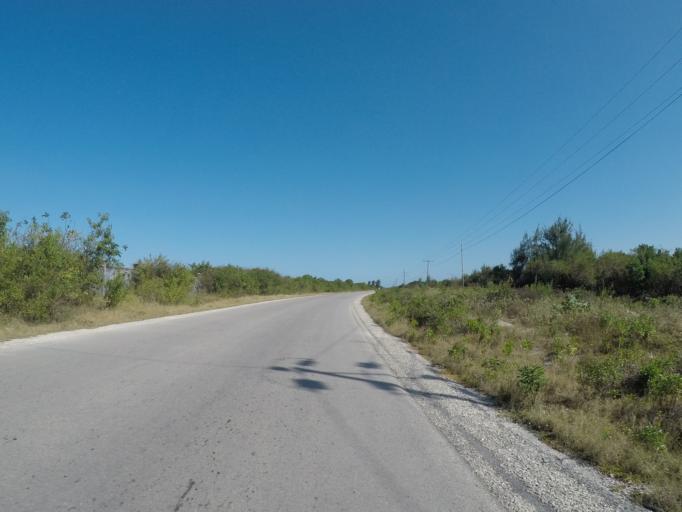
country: TZ
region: Zanzibar Central/South
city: Nganane
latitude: -6.1700
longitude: 39.5260
